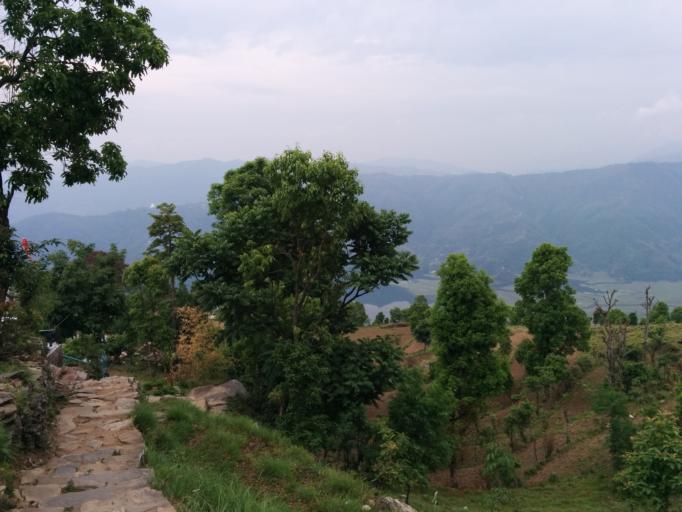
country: NP
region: Western Region
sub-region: Gandaki Zone
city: Pokhara
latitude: 28.2407
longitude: 83.9501
